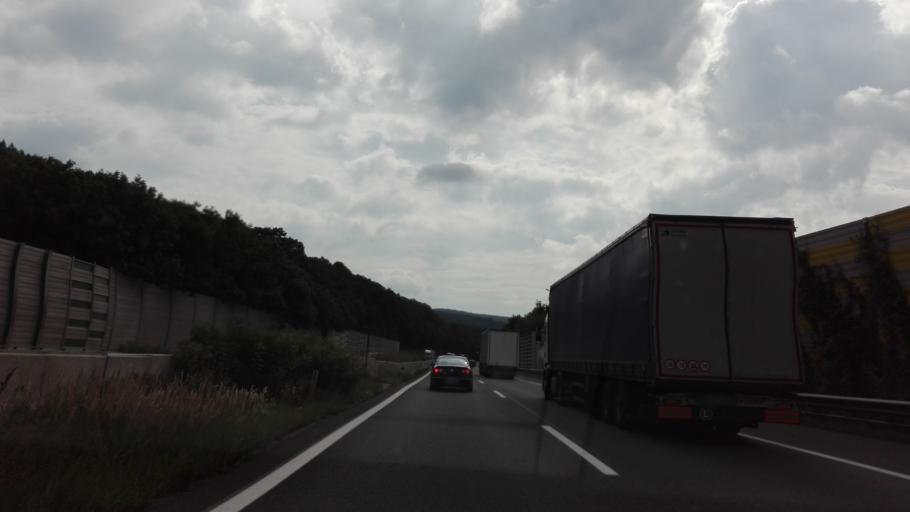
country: AT
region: Lower Austria
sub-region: Politischer Bezirk Baden
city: Klausen-Leopoldsdorf
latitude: 48.0868
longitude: 16.0158
